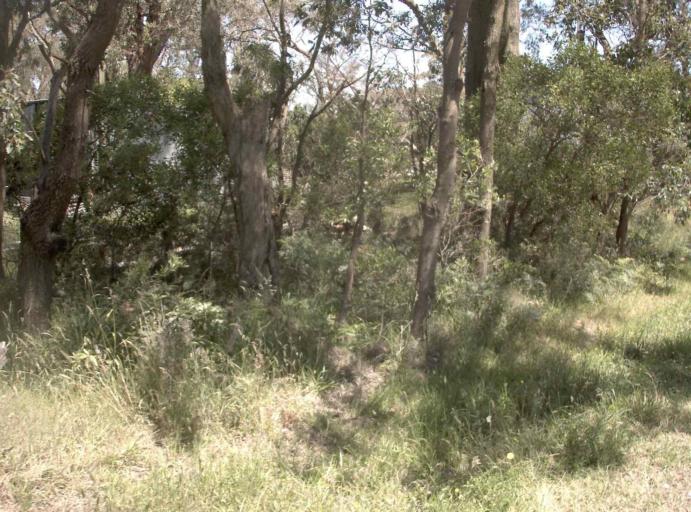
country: AU
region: Victoria
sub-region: Bass Coast
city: North Wonthaggi
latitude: -38.7582
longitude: 146.0711
